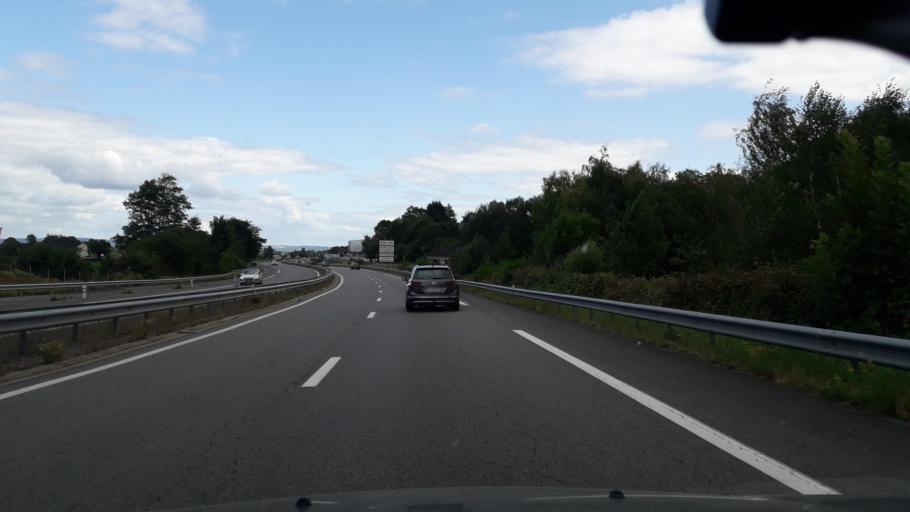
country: FR
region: Limousin
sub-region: Departement de la Creuse
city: Saint-Sulpice-le-Gueretois
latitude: 46.1861
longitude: 1.8247
